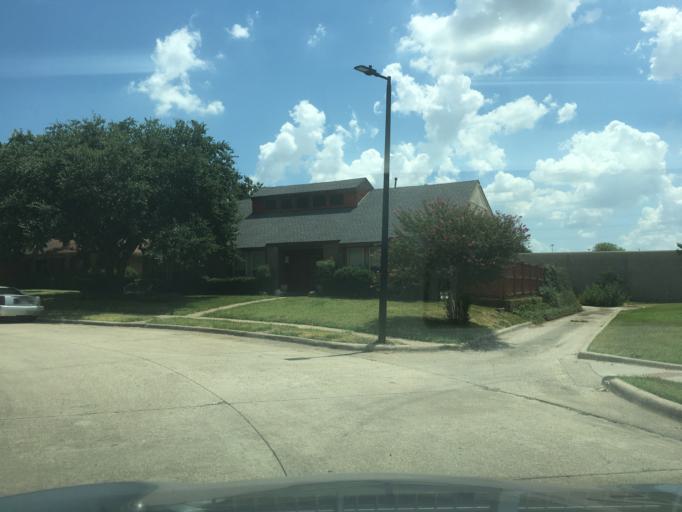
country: US
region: Texas
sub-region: Dallas County
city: Garland
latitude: 32.8659
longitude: -96.6556
